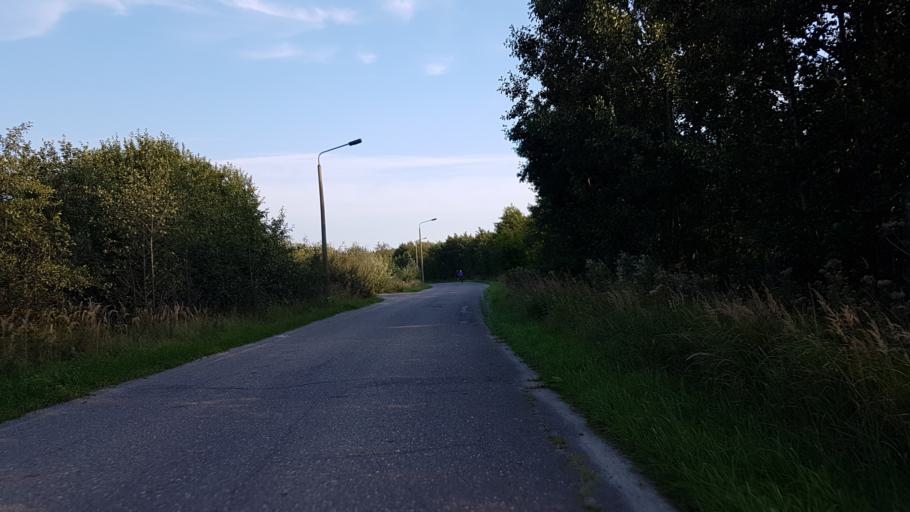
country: DE
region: Mecklenburg-Vorpommern
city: Sagard
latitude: 54.4963
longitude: 13.5520
